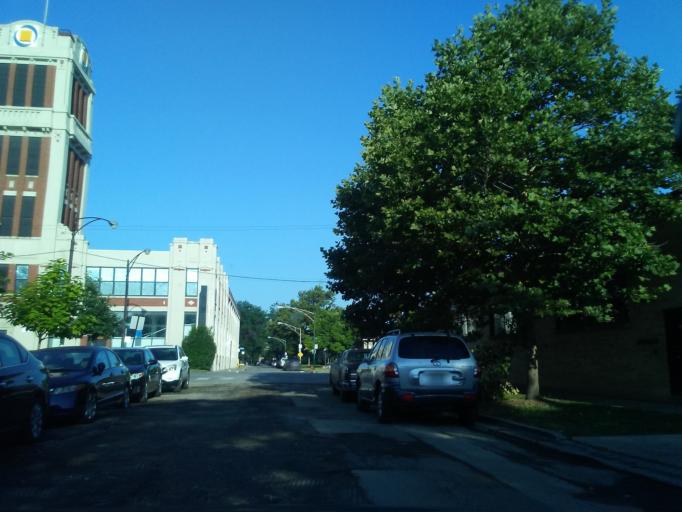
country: US
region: Illinois
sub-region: Cook County
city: Lincolnwood
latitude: 41.9336
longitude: -87.7265
